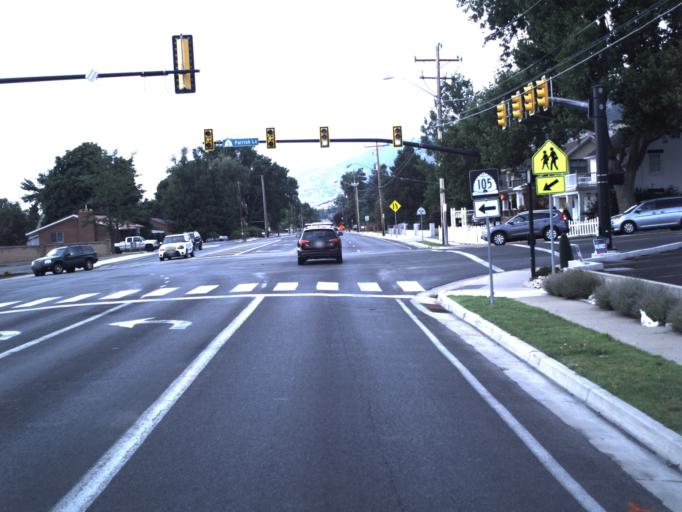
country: US
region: Utah
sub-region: Davis County
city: Centerville
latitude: 40.9211
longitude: -111.8789
